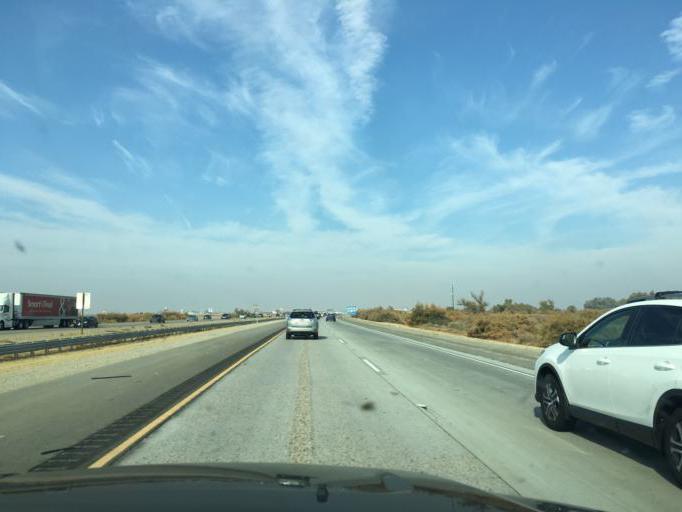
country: US
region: California
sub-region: Kern County
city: Lost Hills
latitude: 35.6059
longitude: -119.6453
